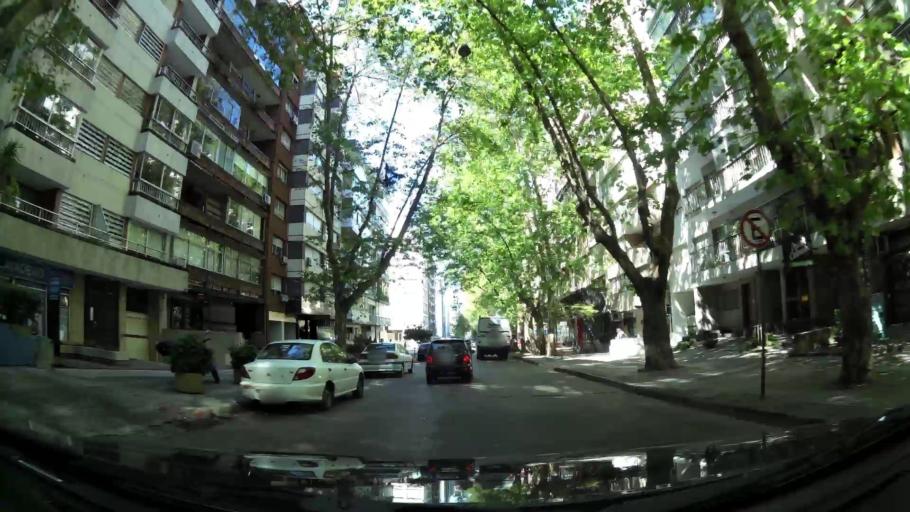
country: UY
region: Montevideo
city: Montevideo
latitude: -34.9117
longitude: -56.1467
